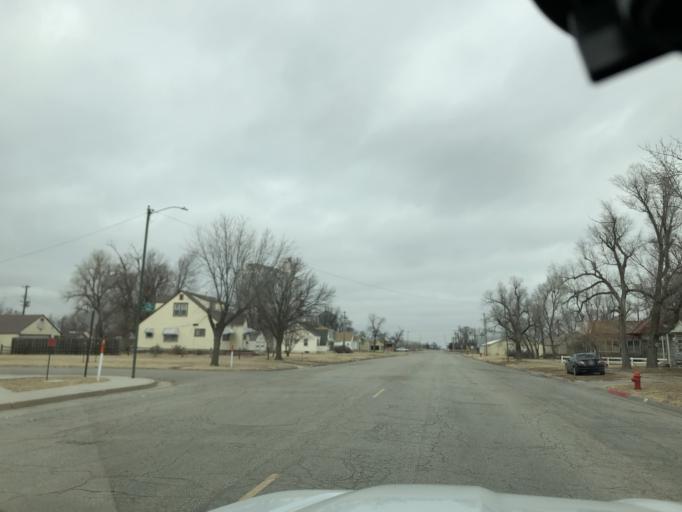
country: US
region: Kansas
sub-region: Stafford County
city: Stafford
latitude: 37.9659
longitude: -98.6005
